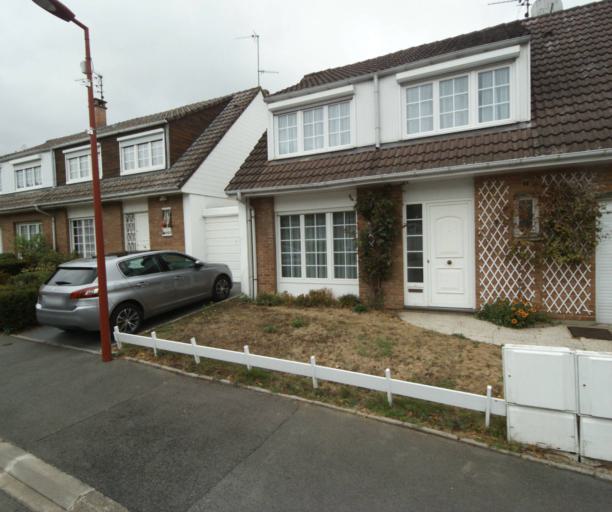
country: FR
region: Nord-Pas-de-Calais
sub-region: Departement du Nord
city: Leers
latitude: 50.6843
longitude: 3.2443
